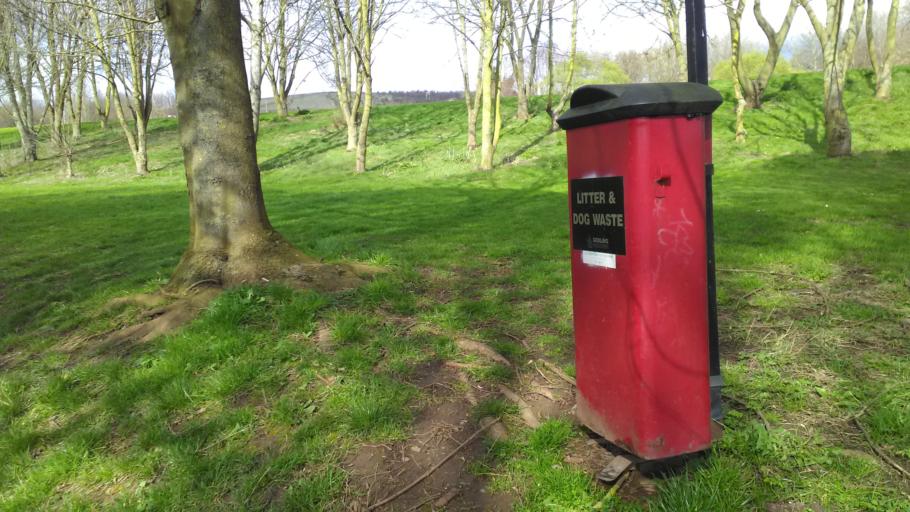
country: GB
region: England
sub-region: Nottinghamshire
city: Burton Joyce
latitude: 52.9813
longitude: -1.0830
